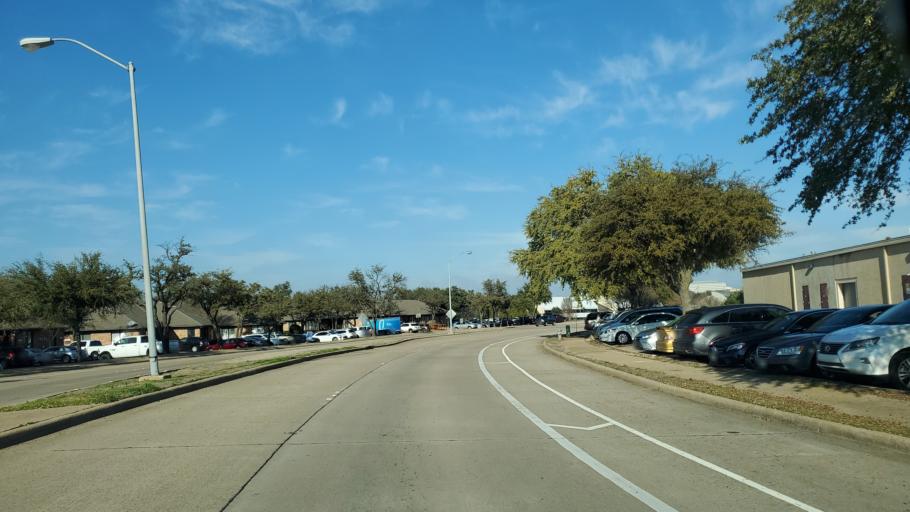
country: US
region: Texas
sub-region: Dallas County
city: Richardson
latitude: 32.9761
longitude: -96.7234
